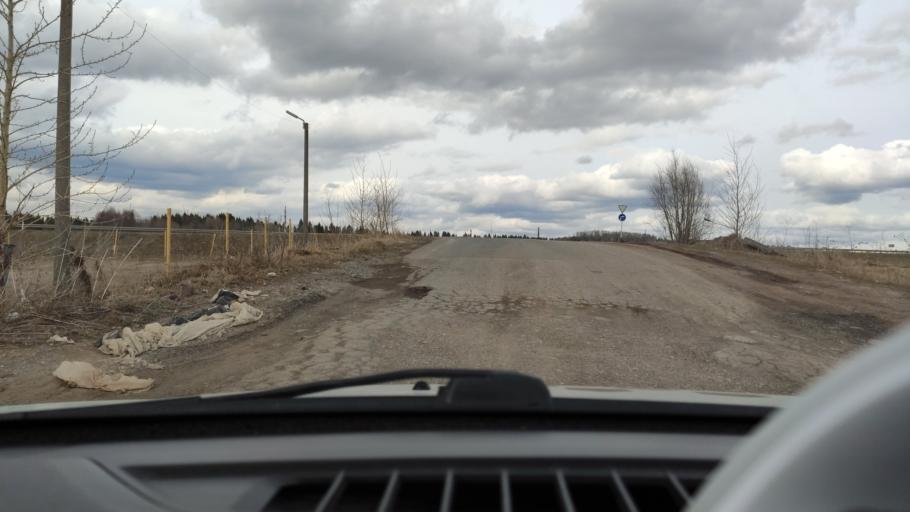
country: RU
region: Perm
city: Froly
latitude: 57.9335
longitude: 56.2375
